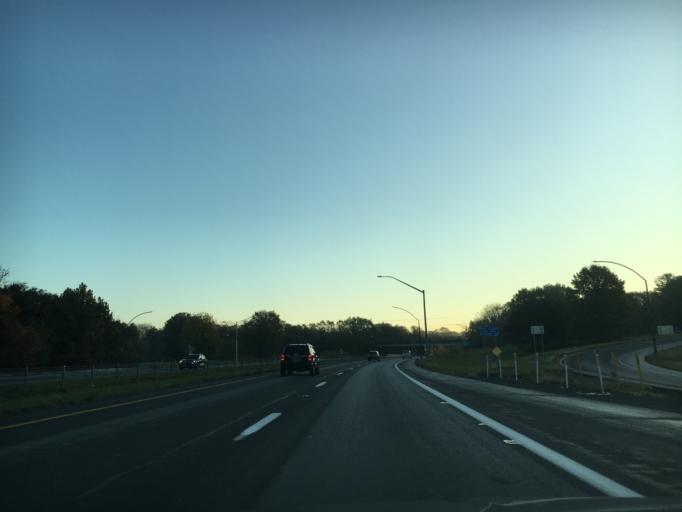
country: US
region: Pennsylvania
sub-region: Lehigh County
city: Fountain Hill
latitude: 40.6274
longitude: -75.3981
